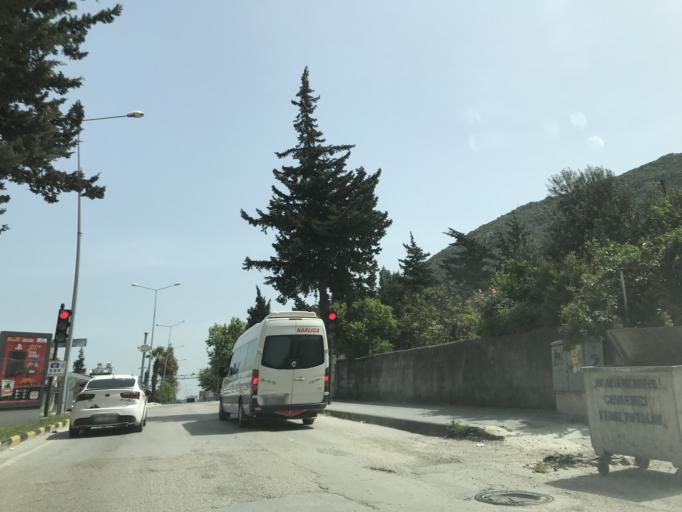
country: TR
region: Hatay
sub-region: Antakya Ilcesi
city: Antakya
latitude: 36.2108
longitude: 36.1747
